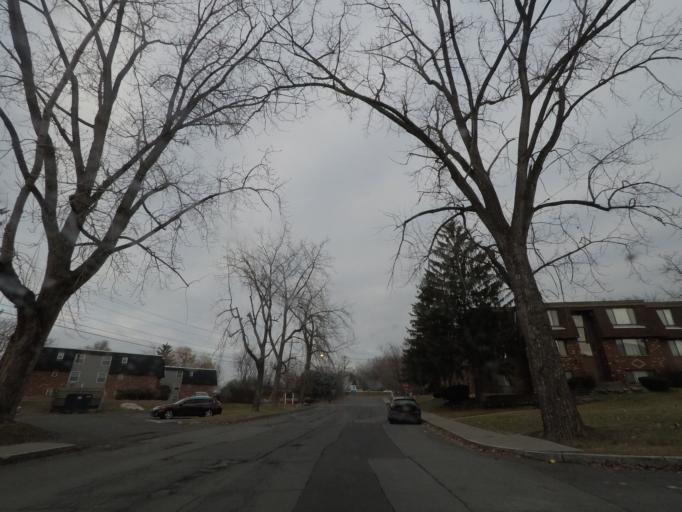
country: US
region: New York
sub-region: Albany County
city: Green Island
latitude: 42.7407
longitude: -73.6695
